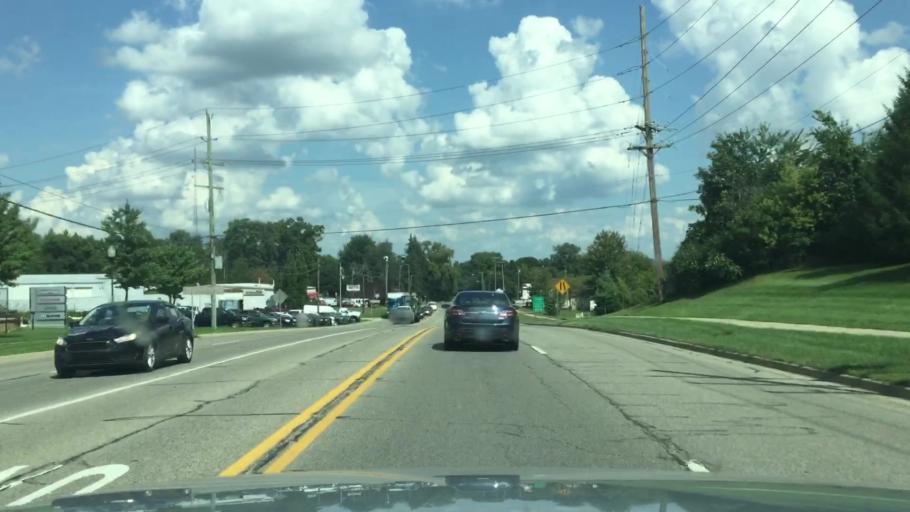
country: US
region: Michigan
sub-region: Washtenaw County
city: Saline
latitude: 42.1604
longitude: -83.7970
